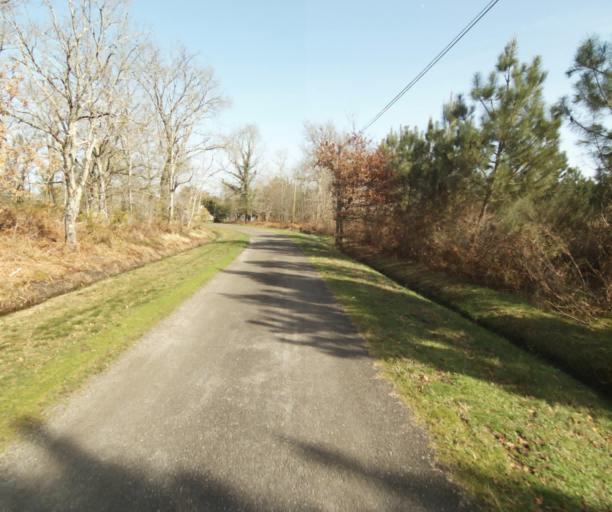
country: FR
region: Aquitaine
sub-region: Departement des Landes
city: Roquefort
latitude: 44.1324
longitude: -0.2100
